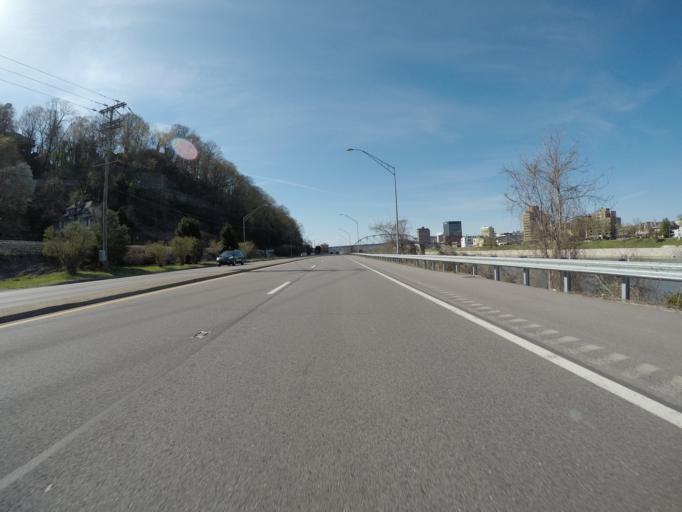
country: US
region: West Virginia
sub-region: Kanawha County
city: Charleston
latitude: 38.3426
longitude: -81.6339
